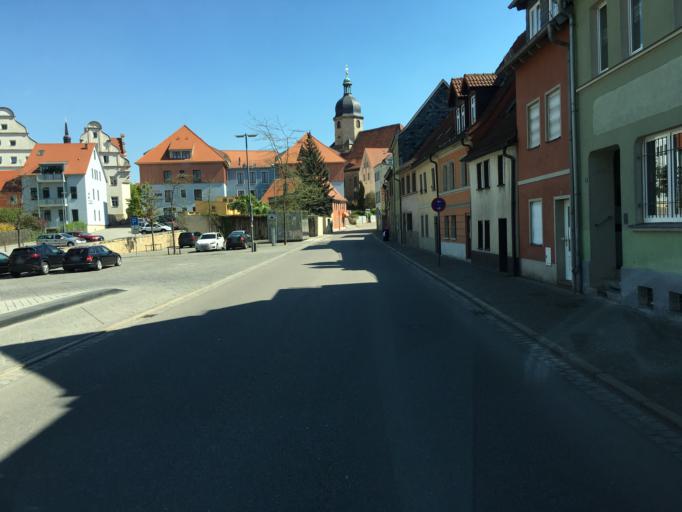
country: DE
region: Saxony-Anhalt
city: Naumburg
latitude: 51.1535
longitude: 11.8035
